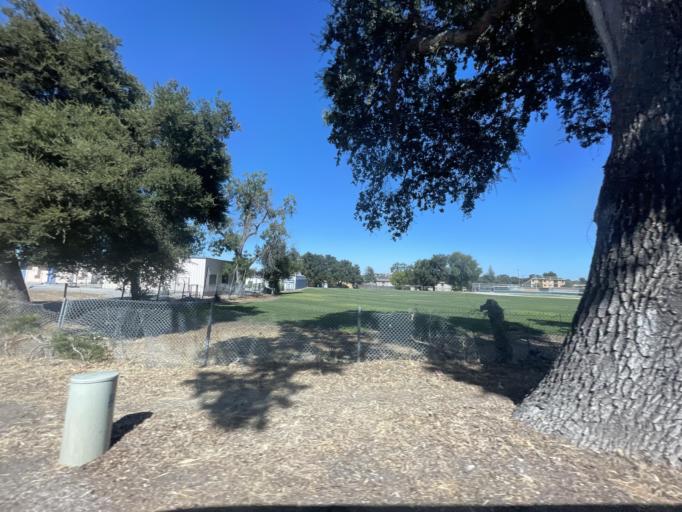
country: US
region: California
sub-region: San Luis Obispo County
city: Paso Robles
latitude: 35.6426
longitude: -120.6953
